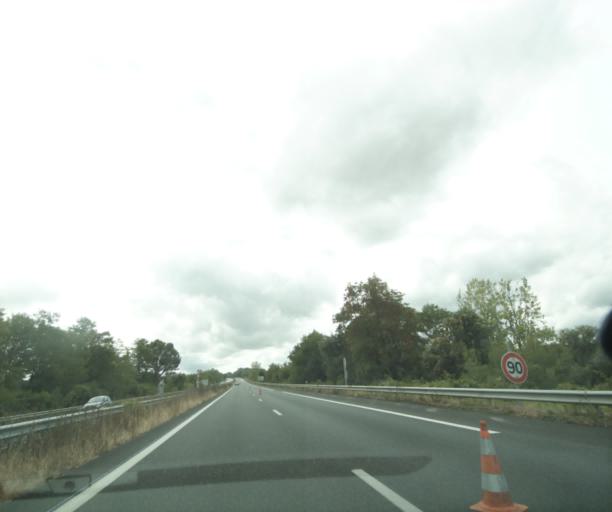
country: FR
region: Poitou-Charentes
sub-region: Departement de la Charente-Maritime
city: Mirambeau
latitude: 45.3631
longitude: -0.5885
